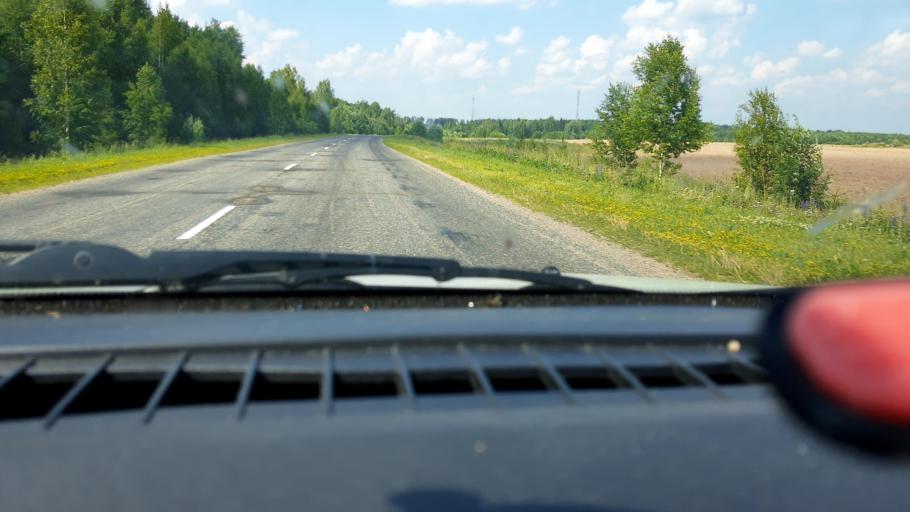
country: RU
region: Nizjnij Novgorod
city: Tonkino
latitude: 57.3590
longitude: 46.4265
